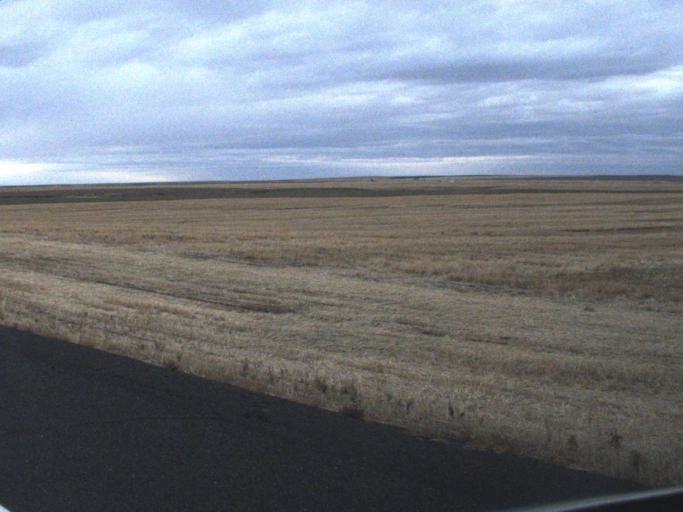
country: US
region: Washington
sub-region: Adams County
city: Ritzville
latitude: 46.7955
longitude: -118.4711
